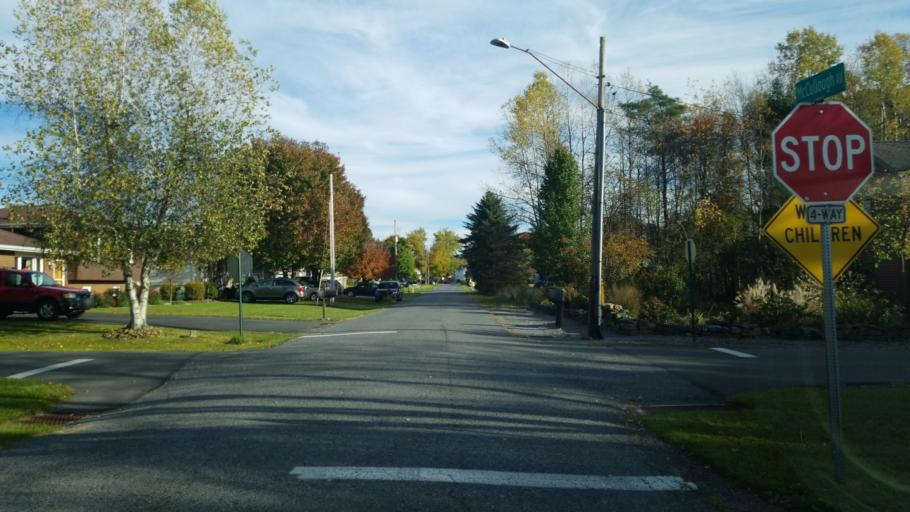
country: US
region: Pennsylvania
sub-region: Jefferson County
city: Brockway
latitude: 41.2498
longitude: -78.7879
